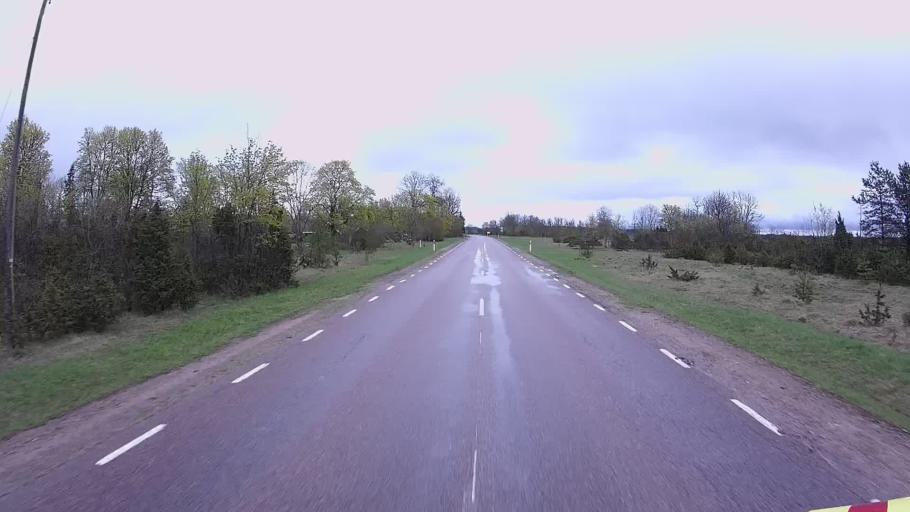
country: EE
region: Saare
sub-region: Kuressaare linn
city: Kuressaare
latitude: 58.3254
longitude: 22.5546
